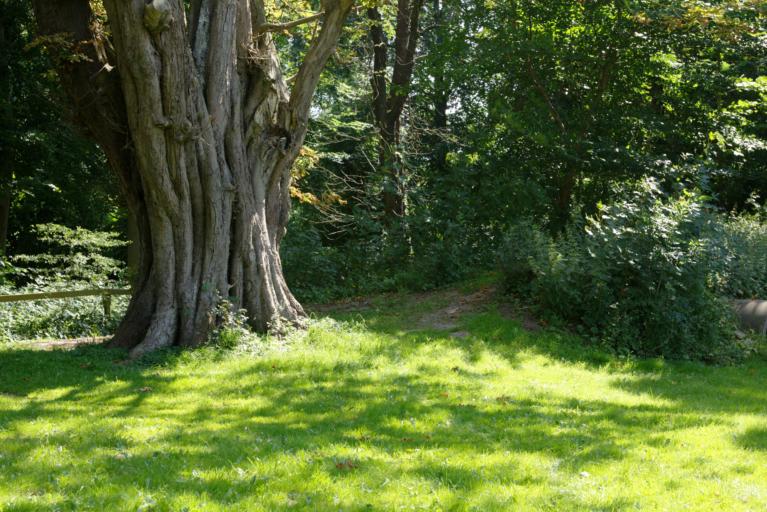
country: DK
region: South Denmark
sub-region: Odense Kommune
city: Neder Holluf
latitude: 55.3810
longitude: 10.4453
